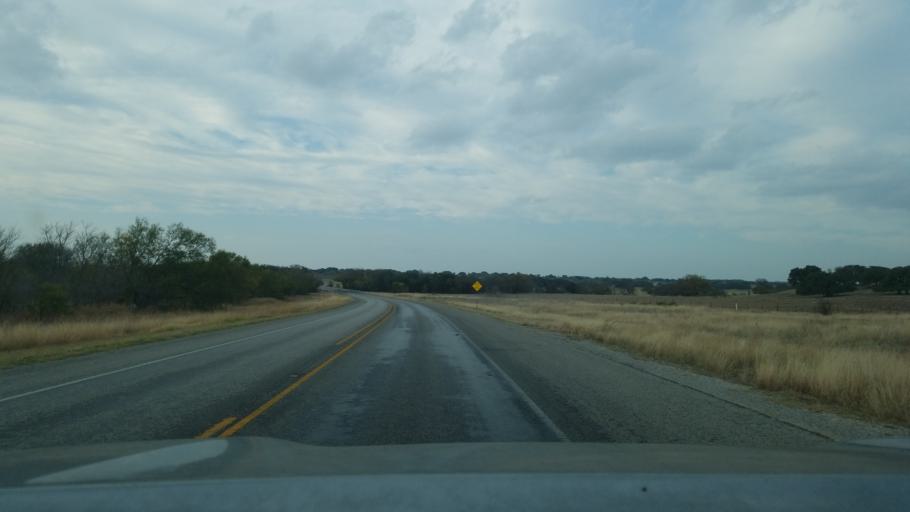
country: US
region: Texas
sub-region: Mills County
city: Goldthwaite
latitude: 31.5105
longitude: -98.5834
